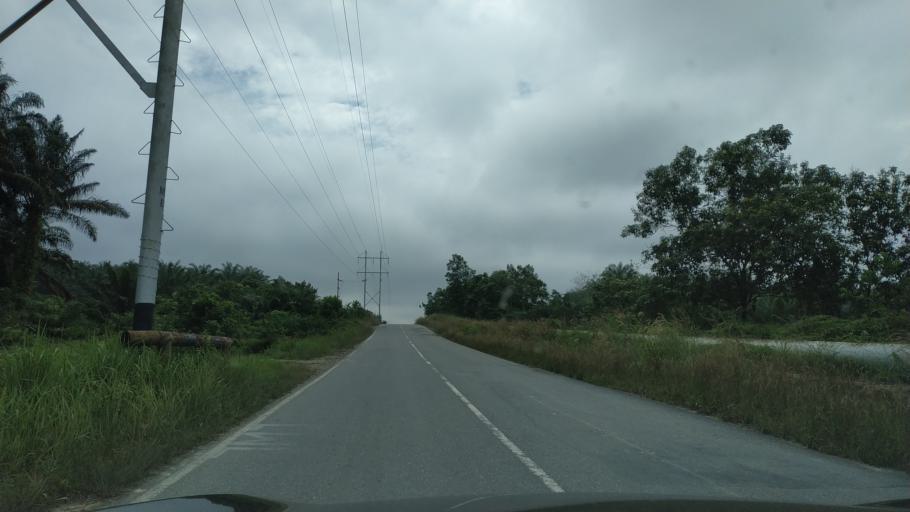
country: ID
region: Riau
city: Pekanbaru
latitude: 0.6435
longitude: 101.6743
